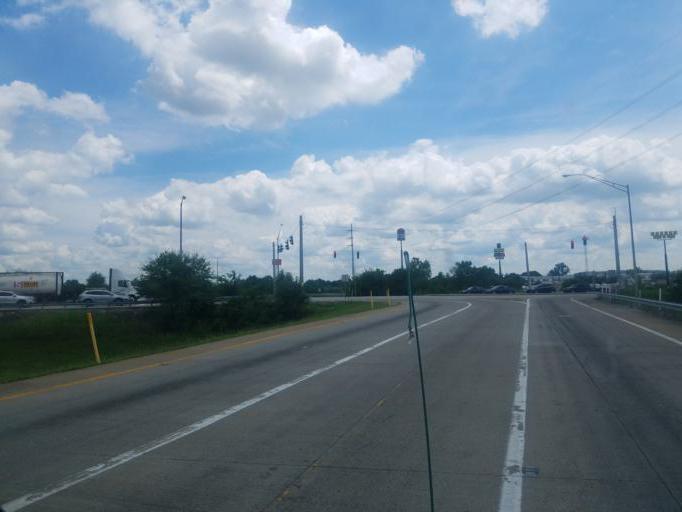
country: US
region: Kentucky
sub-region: Bullitt County
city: Brooks
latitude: 38.0635
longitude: -85.7008
